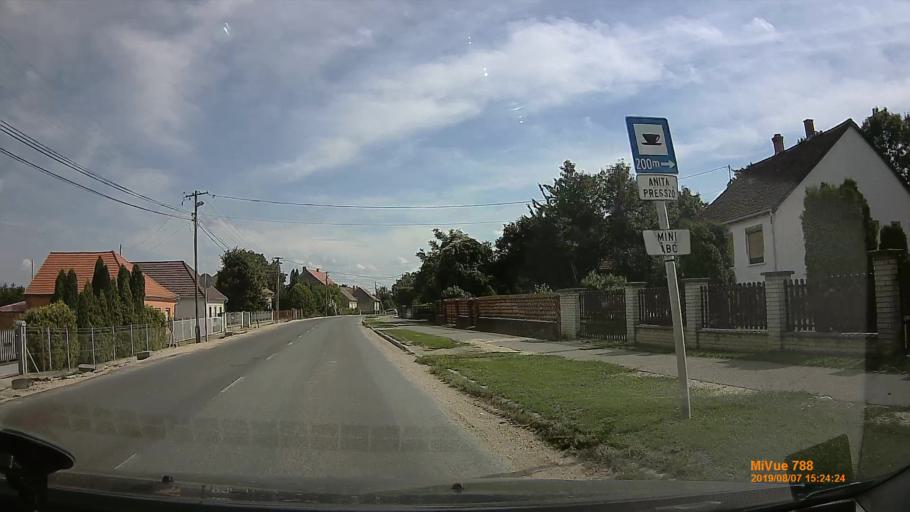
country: HU
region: Vas
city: Buk
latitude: 47.3117
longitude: 16.8319
